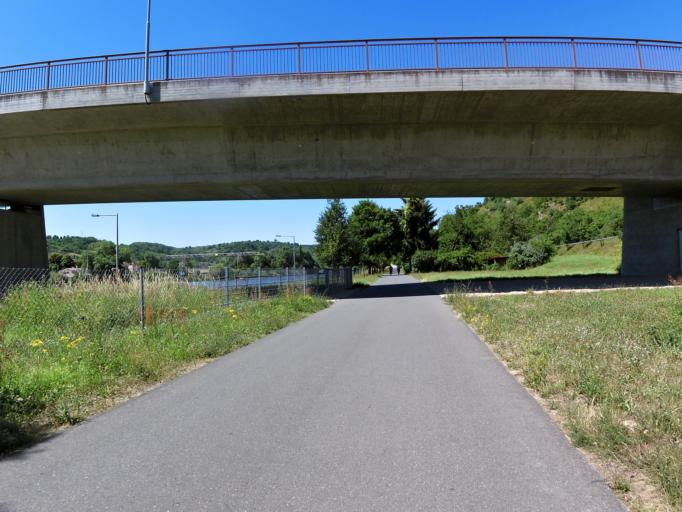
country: DE
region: Bavaria
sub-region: Regierungsbezirk Unterfranken
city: Sommerhausen
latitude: 49.6788
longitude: 10.0383
